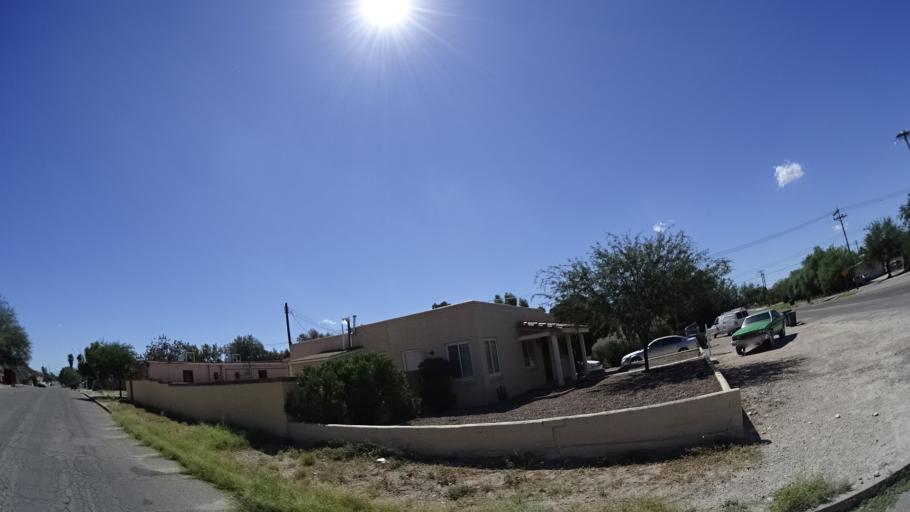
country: US
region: Arizona
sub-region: Pima County
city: Tucson
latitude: 32.2425
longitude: -110.9610
